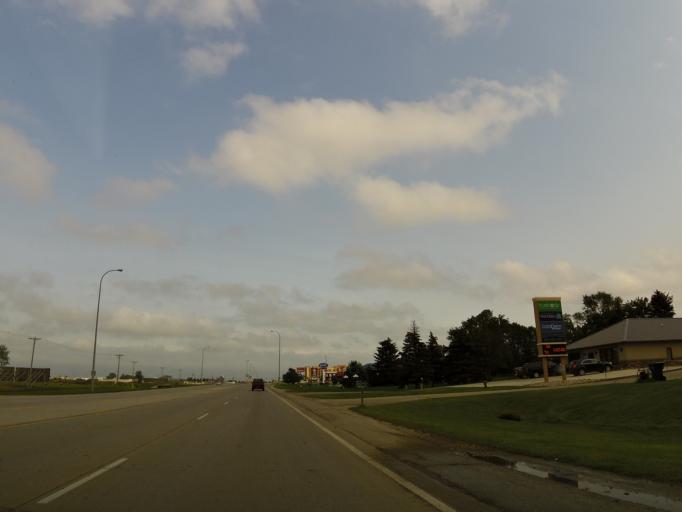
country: US
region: South Dakota
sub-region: Codington County
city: Watertown
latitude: 44.8900
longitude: -97.0766
